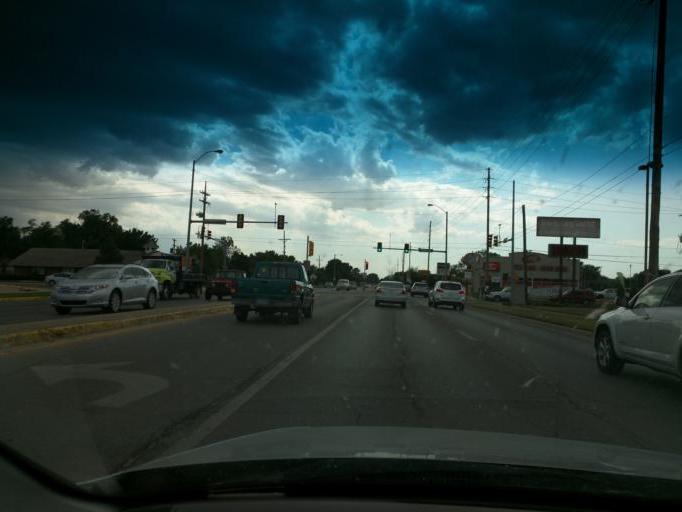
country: US
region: Kansas
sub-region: Reno County
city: Hutchinson
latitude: 38.0867
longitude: -97.9214
